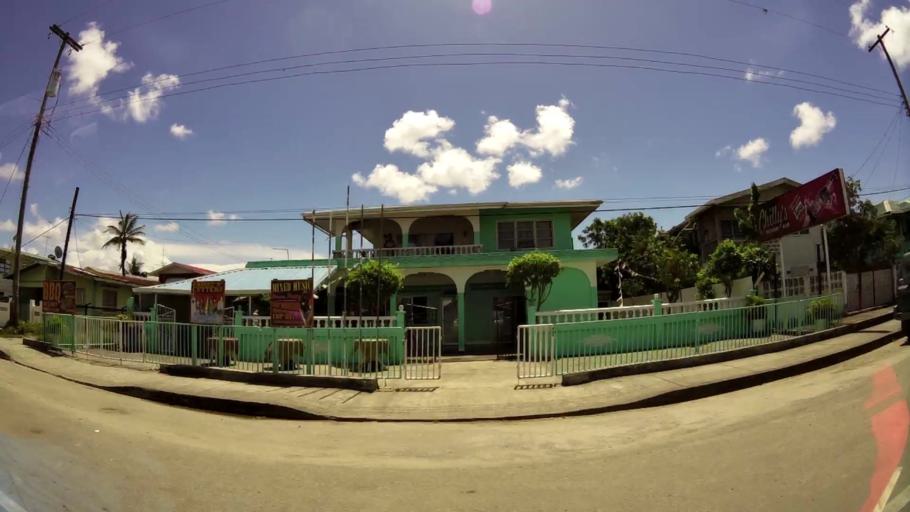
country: GY
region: Demerara-Mahaica
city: Georgetown
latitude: 6.7963
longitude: -58.1688
